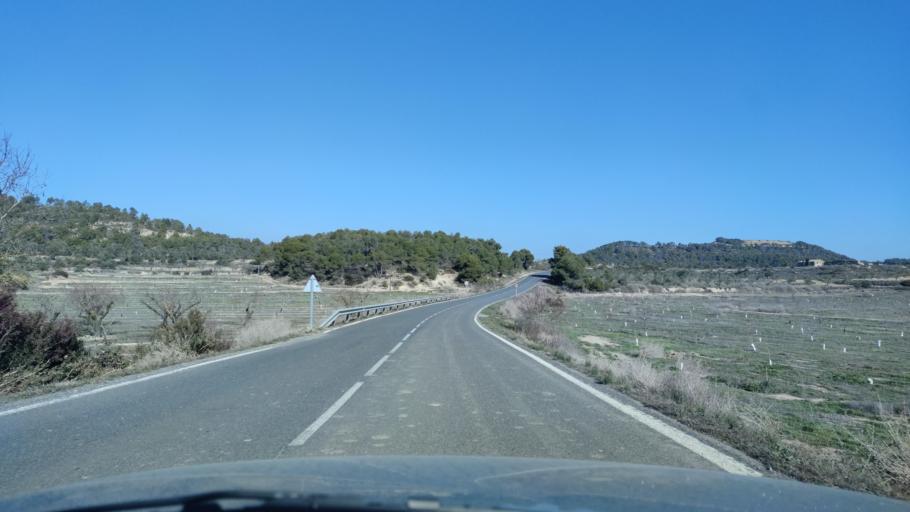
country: ES
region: Catalonia
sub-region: Provincia de Lleida
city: Maials
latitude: 41.3310
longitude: 0.4407
